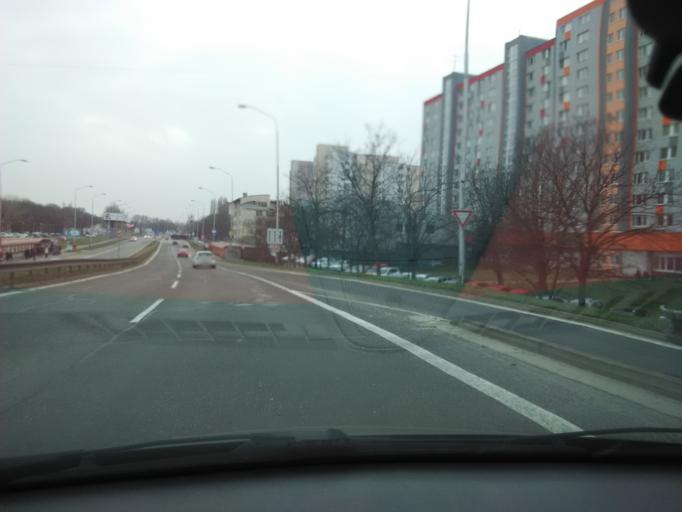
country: SK
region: Bratislavsky
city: Bratislava
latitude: 48.1269
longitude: 17.1302
